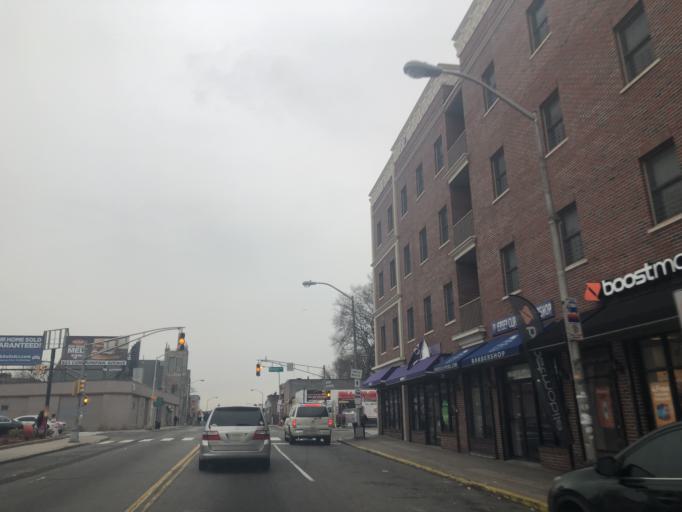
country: US
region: New Jersey
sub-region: Hudson County
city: Jersey City
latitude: 40.7183
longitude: -74.0749
